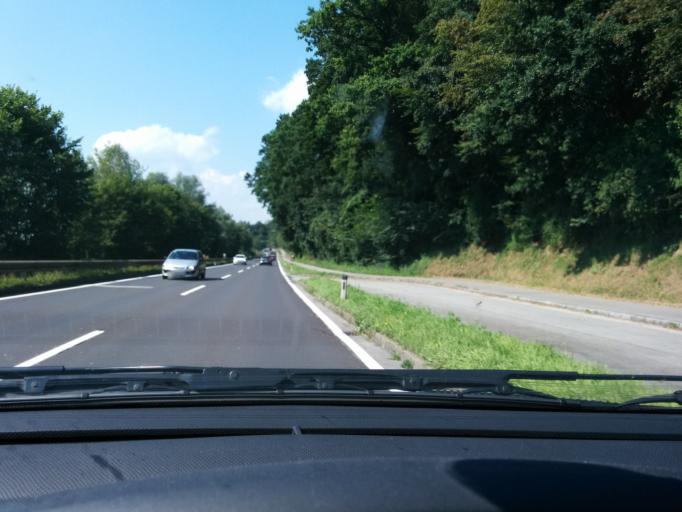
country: AT
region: Upper Austria
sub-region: Politischer Bezirk Urfahr-Umgebung
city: Ottensheim
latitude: 48.3270
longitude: 14.1969
